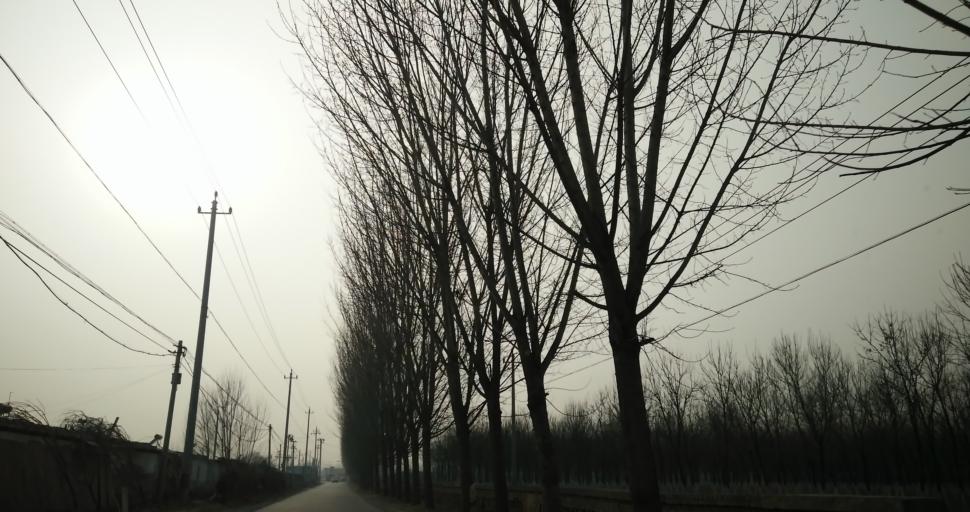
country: CN
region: Beijing
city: Xingfeng
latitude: 39.7123
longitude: 116.3637
